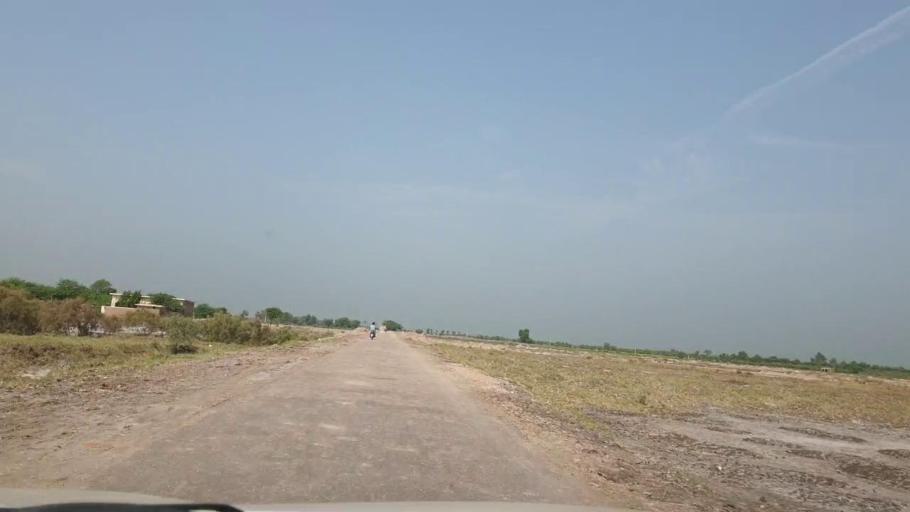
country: PK
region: Sindh
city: Larkana
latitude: 27.4305
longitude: 68.2089
